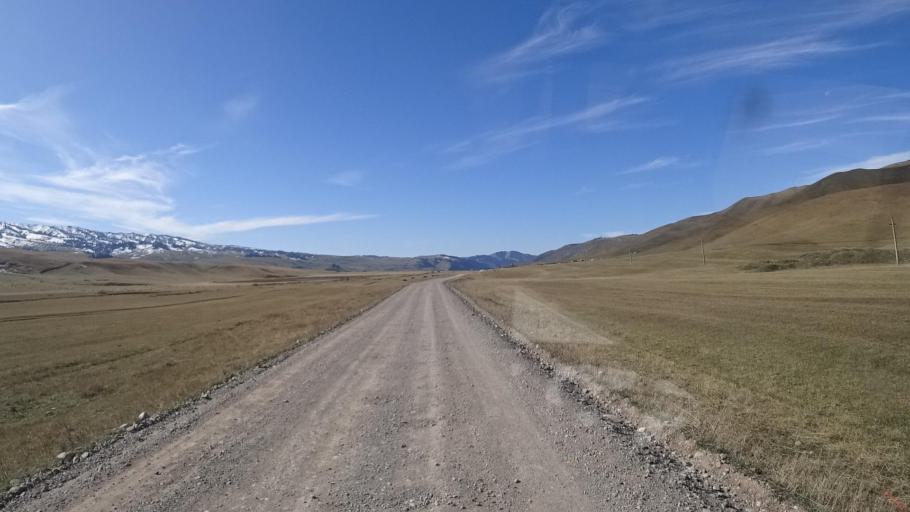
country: KZ
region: Almaty Oblysy
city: Kegen
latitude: 42.7581
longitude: 79.0191
